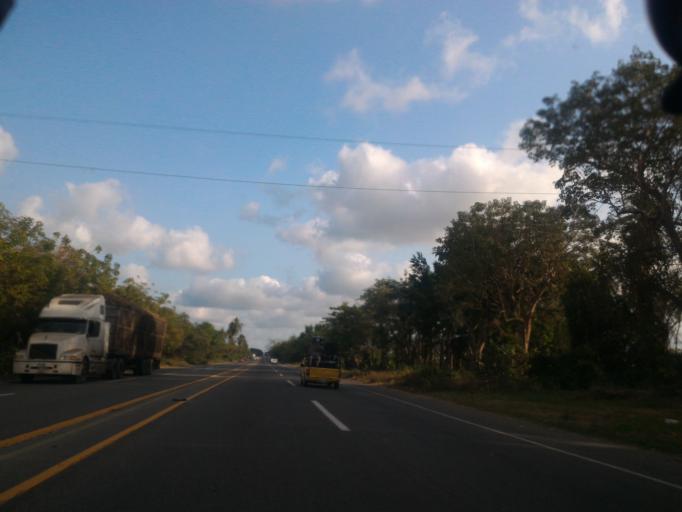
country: MX
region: Colima
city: Tecoman
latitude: 18.8767
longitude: -103.8457
